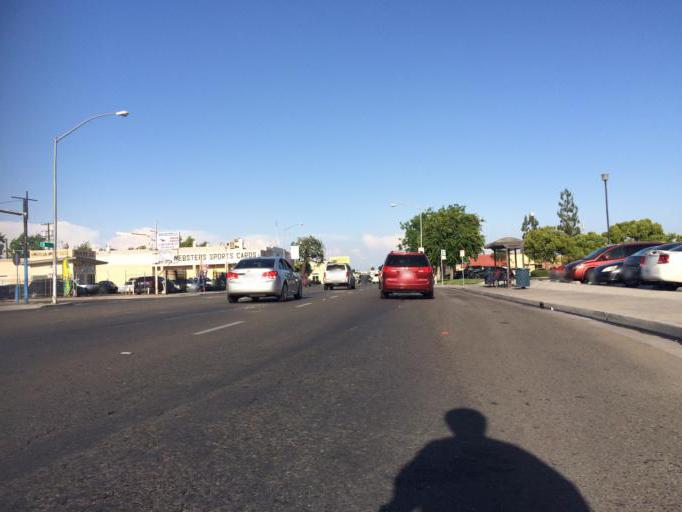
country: US
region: California
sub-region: Fresno County
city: Fresno
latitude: 36.7432
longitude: -119.7715
